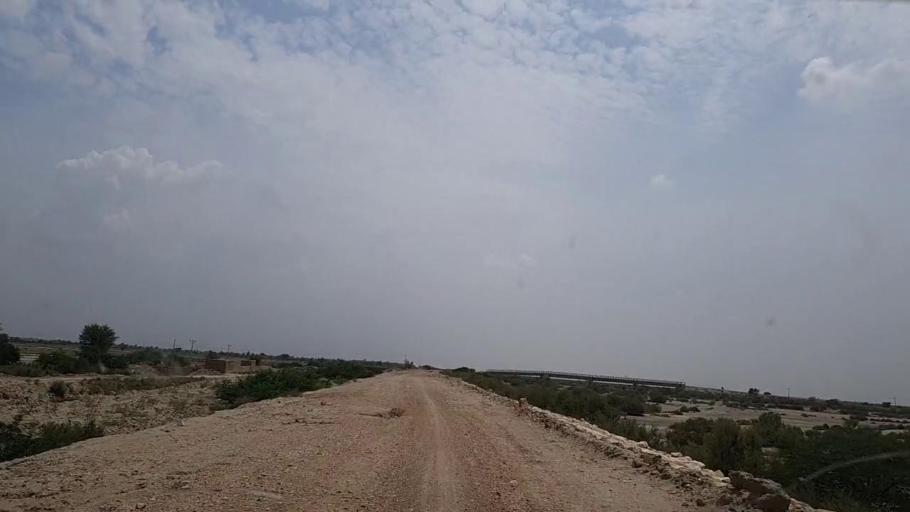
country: PK
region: Sindh
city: Phulji
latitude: 26.8242
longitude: 67.6139
